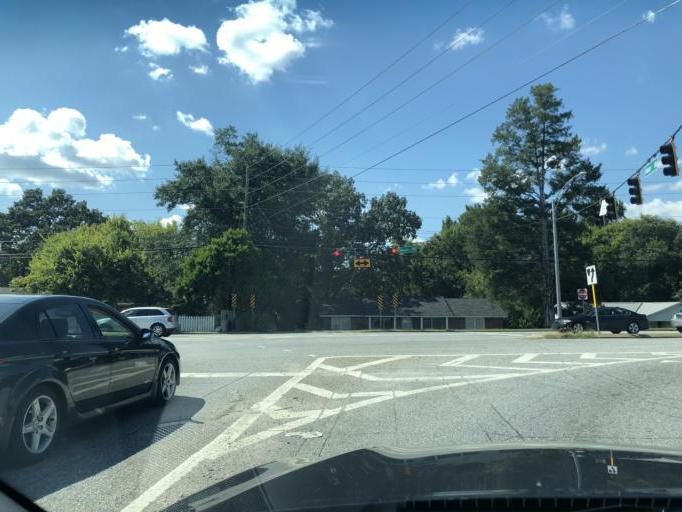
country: US
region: Georgia
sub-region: Muscogee County
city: Columbus
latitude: 32.5278
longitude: -84.9252
